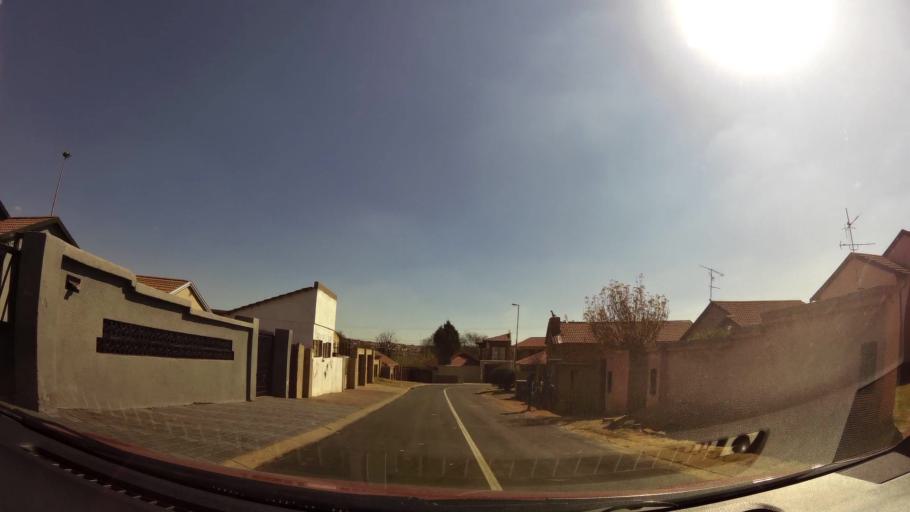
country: ZA
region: Gauteng
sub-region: City of Johannesburg Metropolitan Municipality
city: Soweto
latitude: -26.2367
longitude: 27.8197
